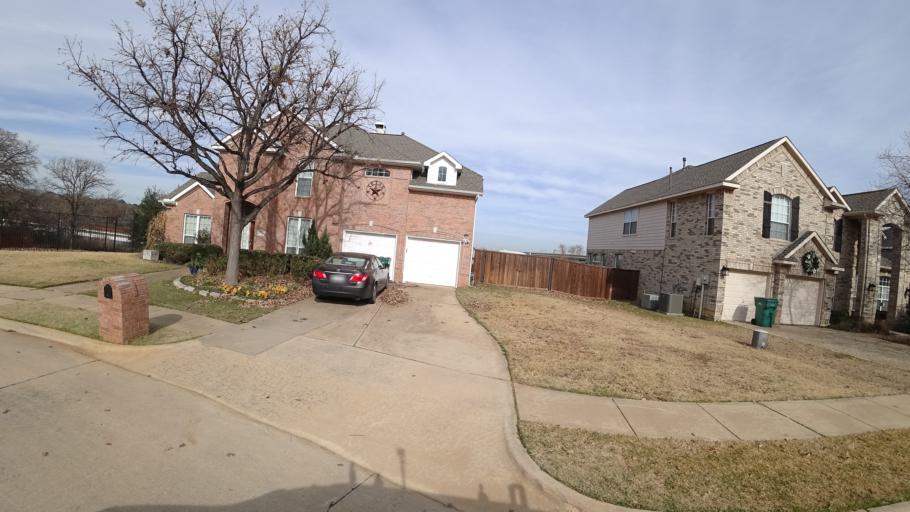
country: US
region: Texas
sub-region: Denton County
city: Highland Village
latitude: 33.0856
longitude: -97.0301
